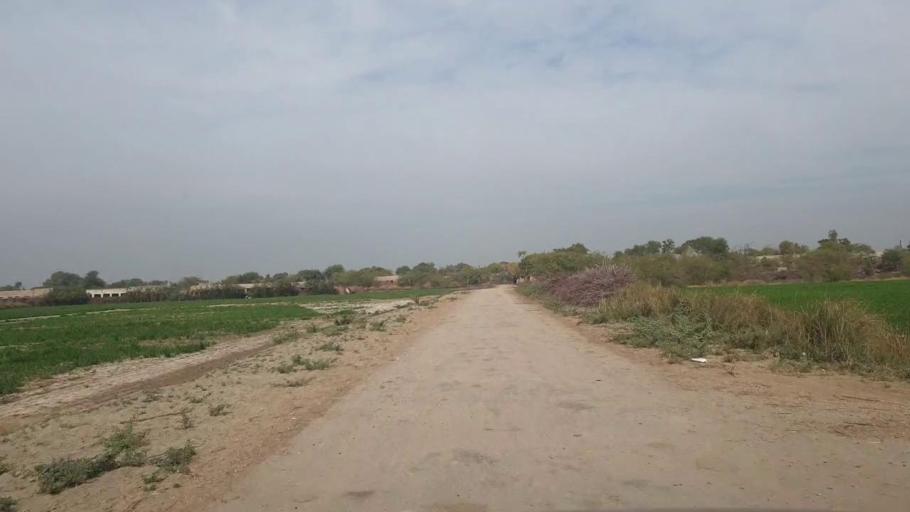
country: PK
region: Sindh
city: Nawabshah
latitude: 26.1247
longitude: 68.4980
